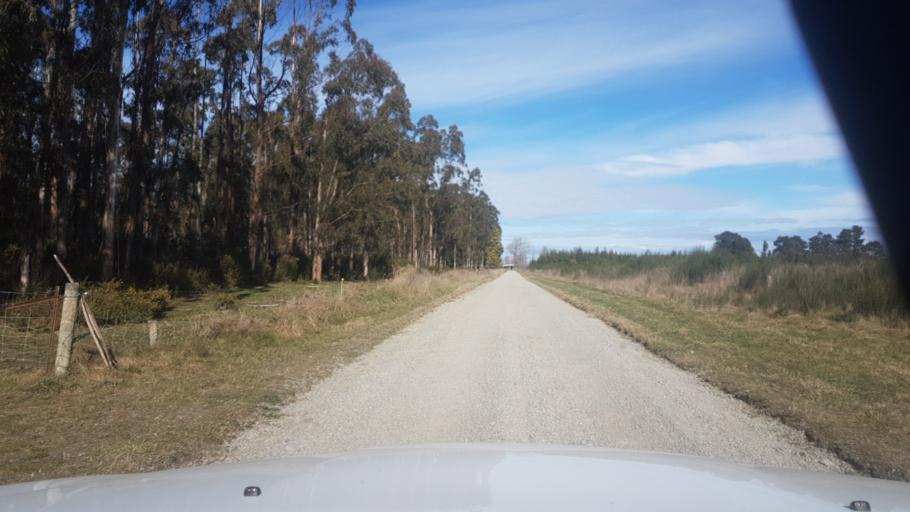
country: NZ
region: Canterbury
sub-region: Timaru District
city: Pleasant Point
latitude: -44.1401
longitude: 171.2758
